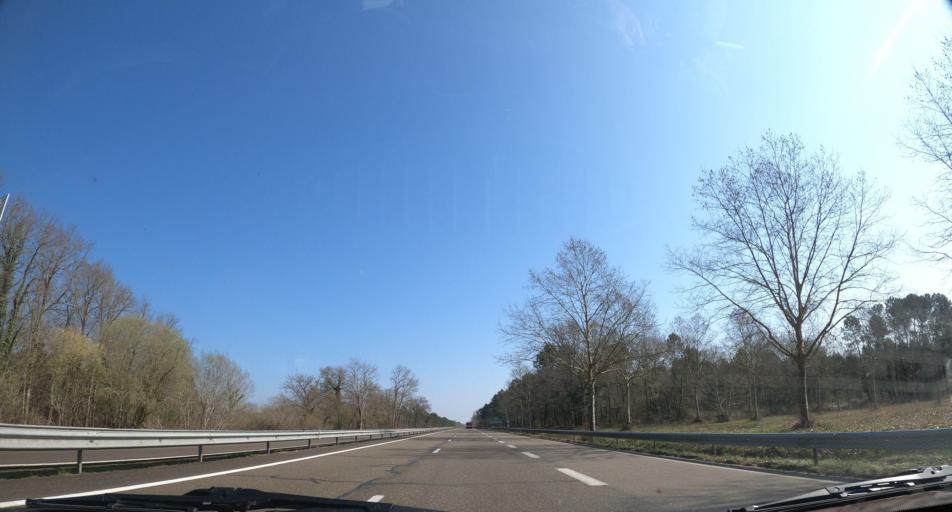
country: FR
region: Aquitaine
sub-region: Departement des Landes
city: Saint-Perdon
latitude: 43.8772
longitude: -0.5605
